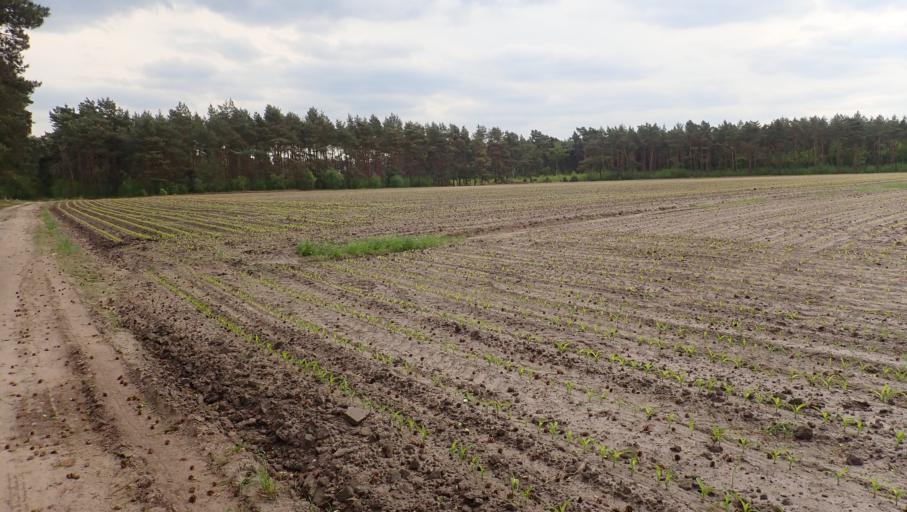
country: BE
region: Flanders
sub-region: Provincie Antwerpen
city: Oostmalle
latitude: 51.2741
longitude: 4.7453
